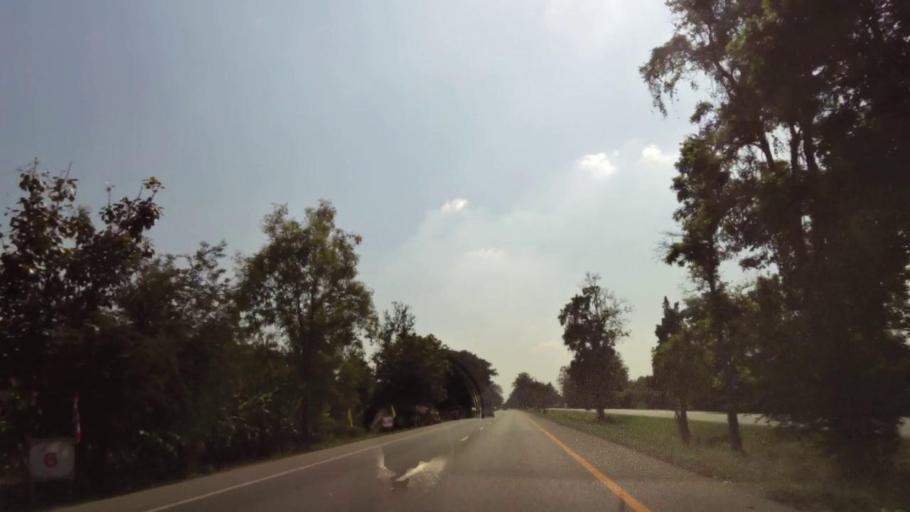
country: TH
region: Phichit
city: Bueng Na Rang
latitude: 16.2360
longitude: 100.1255
